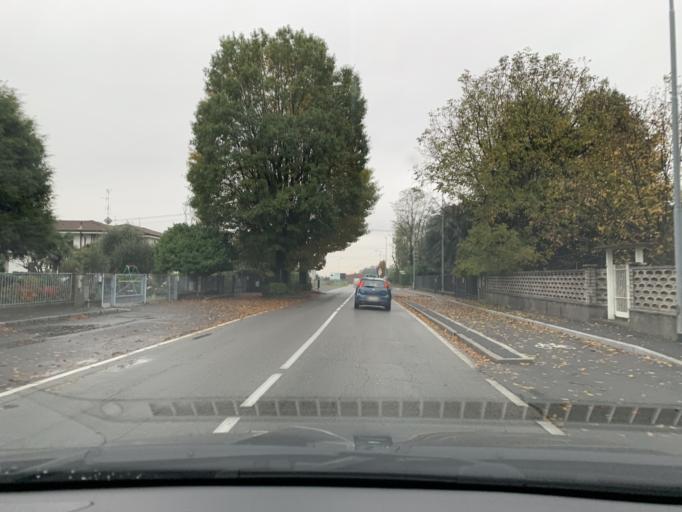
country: IT
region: Lombardy
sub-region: Provincia di Como
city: Rovellasca
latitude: 45.6596
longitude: 9.0530
